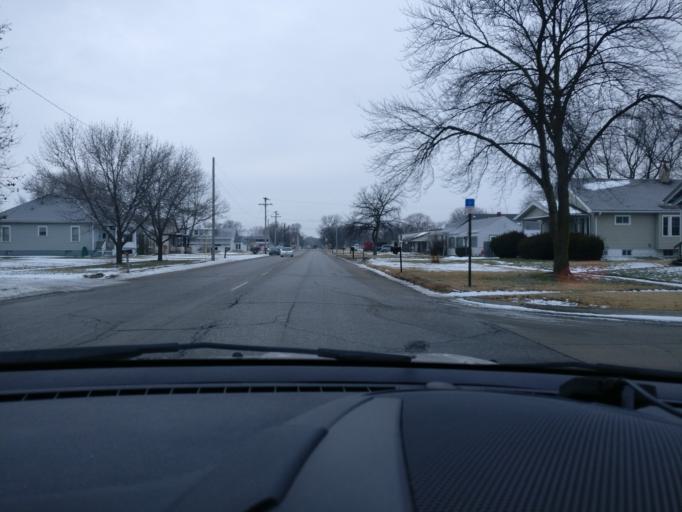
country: US
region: Nebraska
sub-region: Dodge County
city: Fremont
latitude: 41.4364
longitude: -96.5076
